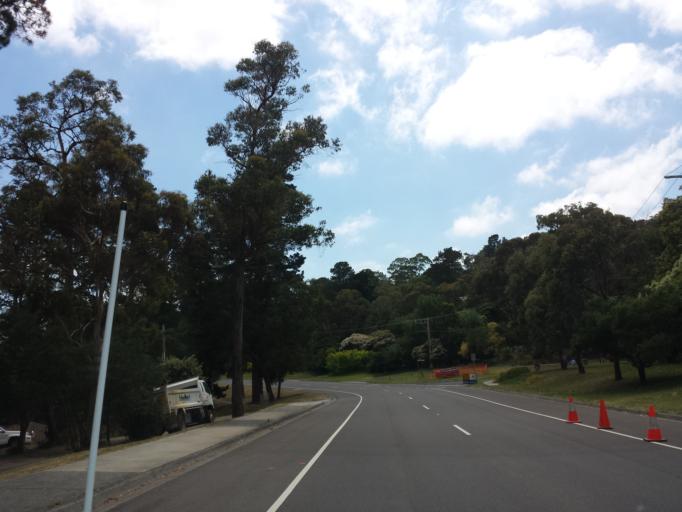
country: AU
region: Victoria
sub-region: Knox
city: Boronia
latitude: -37.8663
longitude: 145.2979
